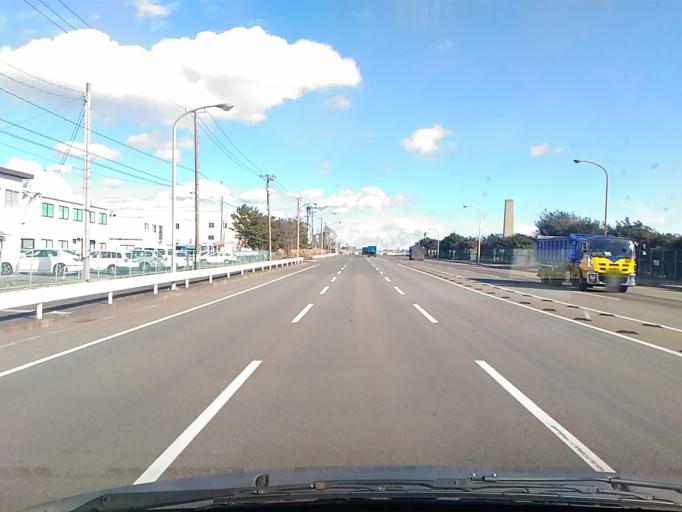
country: JP
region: Fukushima
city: Iwaki
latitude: 36.9335
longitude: 140.8681
